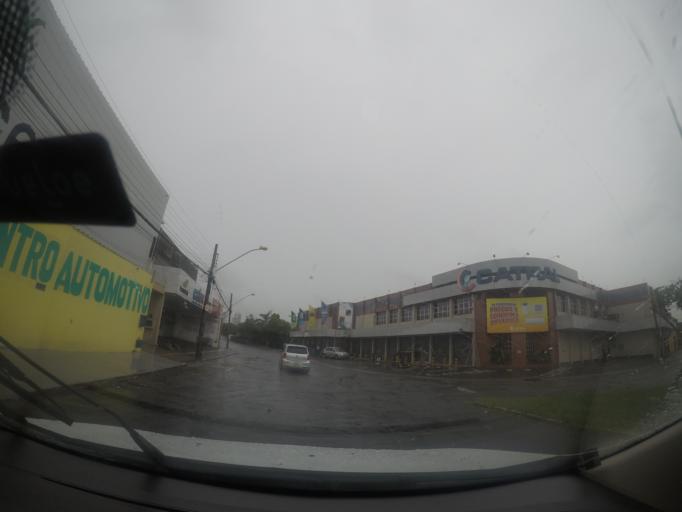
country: BR
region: Goias
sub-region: Goiania
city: Goiania
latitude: -16.6766
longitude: -49.2804
